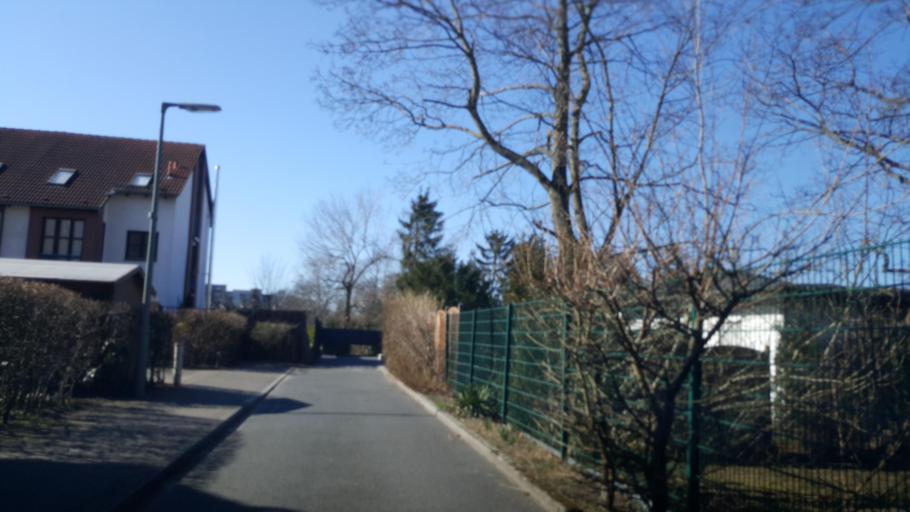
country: DE
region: Berlin
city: Rudow
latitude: 52.4211
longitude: 13.5082
